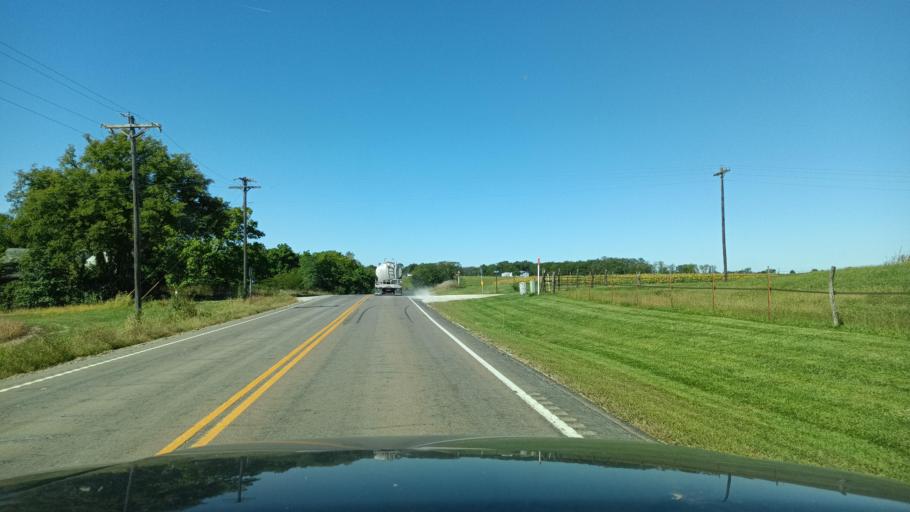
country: US
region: Missouri
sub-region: Scotland County
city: Memphis
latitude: 40.4561
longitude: -92.1334
